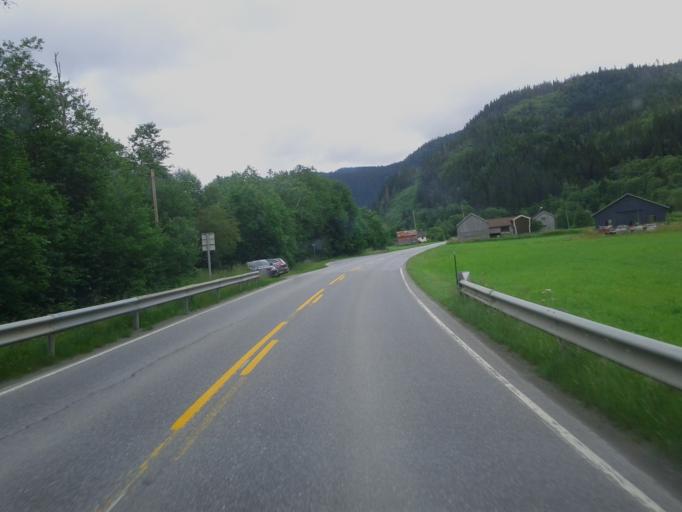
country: NO
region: Sor-Trondelag
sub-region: Midtre Gauldal
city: Storen
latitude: 63.0194
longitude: 10.3302
